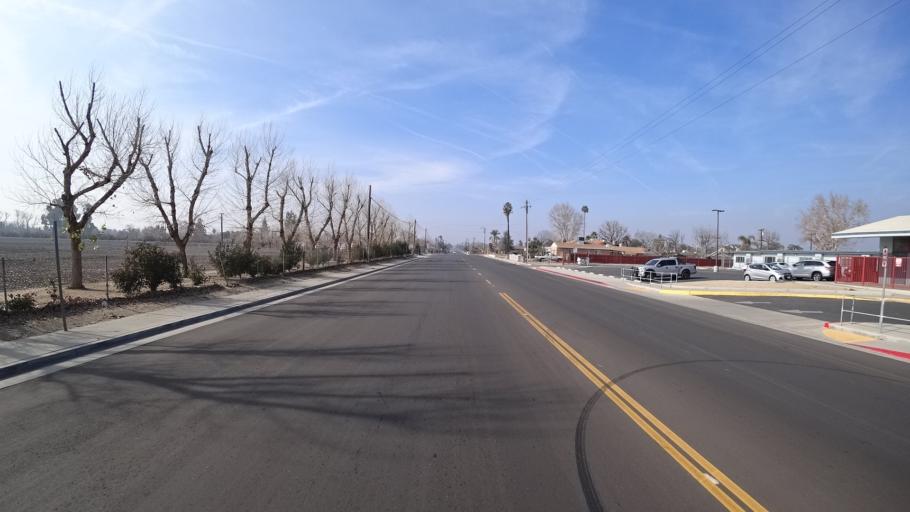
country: US
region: California
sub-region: Kern County
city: Bakersfield
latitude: 35.3465
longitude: -119.0133
